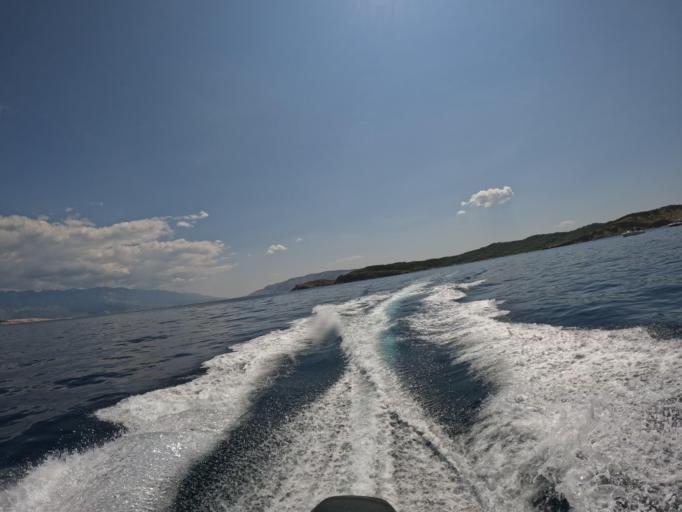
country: HR
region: Primorsko-Goranska
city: Lopar
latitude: 44.8507
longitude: 14.7575
